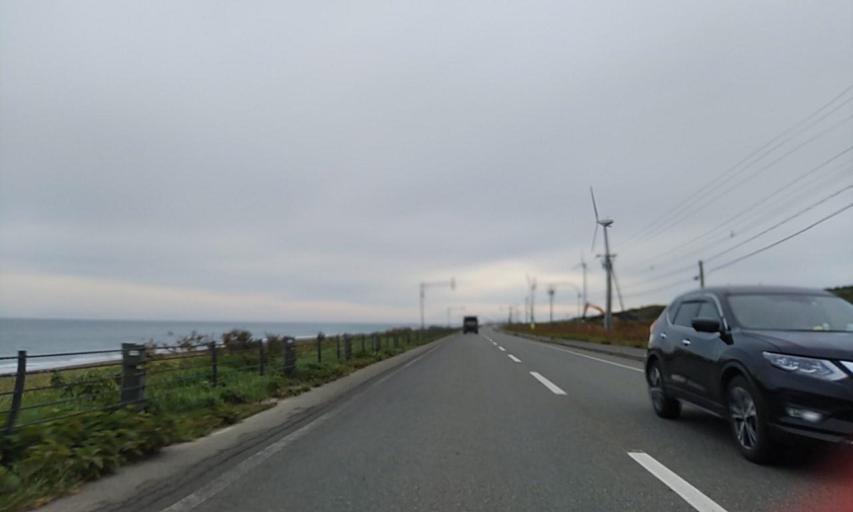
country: JP
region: Hokkaido
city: Makubetsu
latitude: 45.3692
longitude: 142.1094
